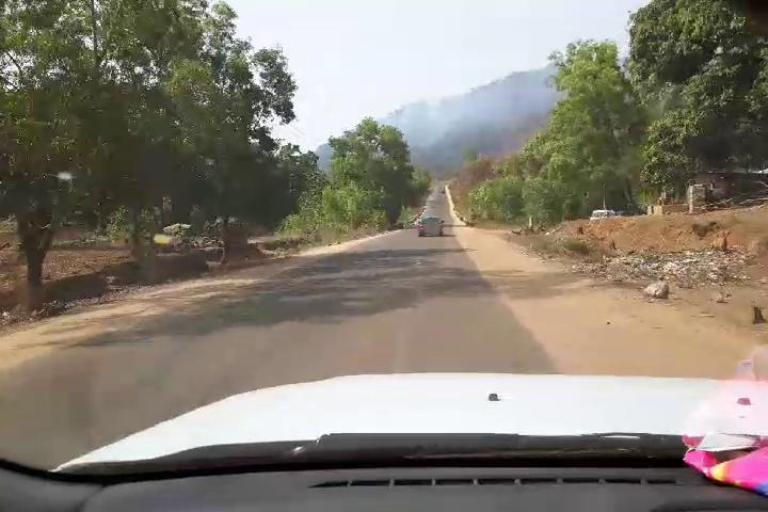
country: SL
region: Western Area
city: Waterloo
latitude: 8.2481
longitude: -13.1526
